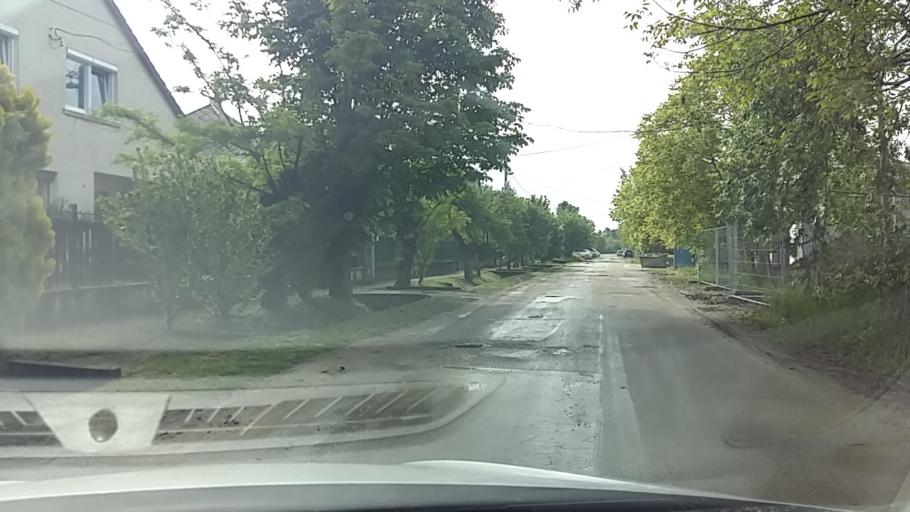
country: HU
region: Budapest
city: Budapest XVI. keruelet
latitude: 47.5030
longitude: 19.2083
